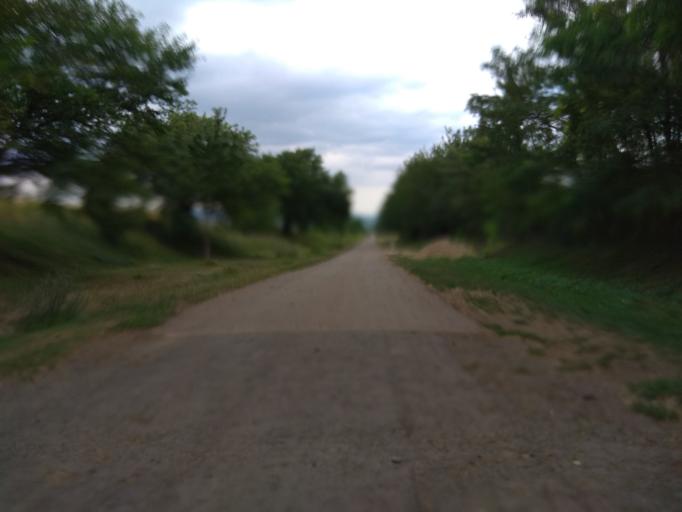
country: HU
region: Borsod-Abauj-Zemplen
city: Megyaszo
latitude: 48.1380
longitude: 21.0133
